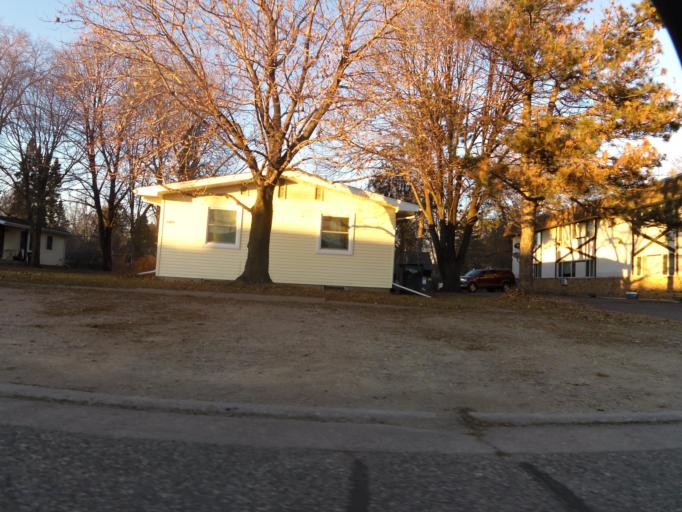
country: US
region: Wisconsin
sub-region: Saint Croix County
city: Hudson
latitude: 44.9641
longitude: -92.7385
